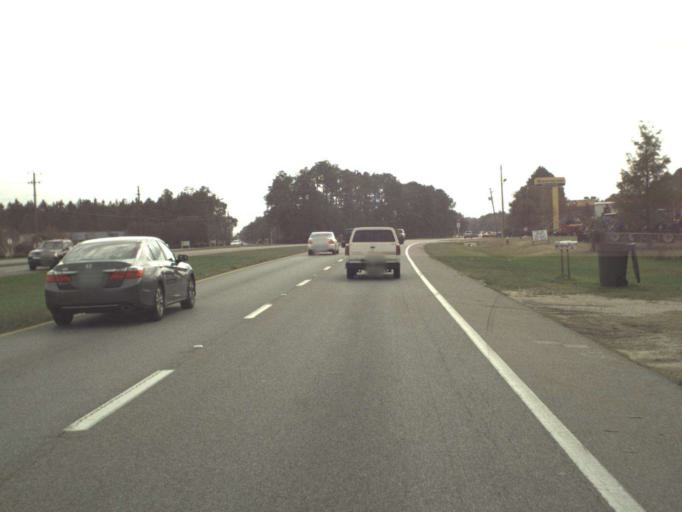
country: US
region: Florida
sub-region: Escambia County
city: Gonzalez
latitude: 30.5522
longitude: -87.2836
